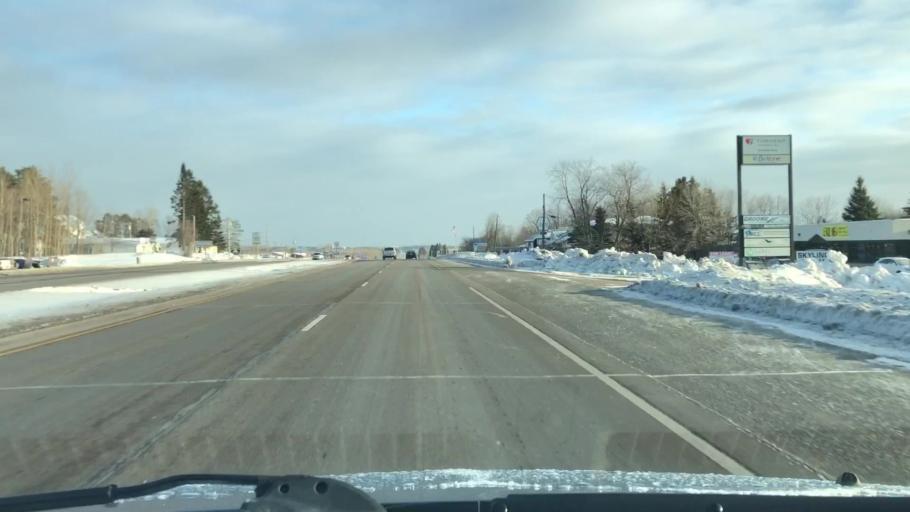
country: US
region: Minnesota
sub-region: Saint Louis County
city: Hermantown
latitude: 46.8265
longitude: -92.1940
